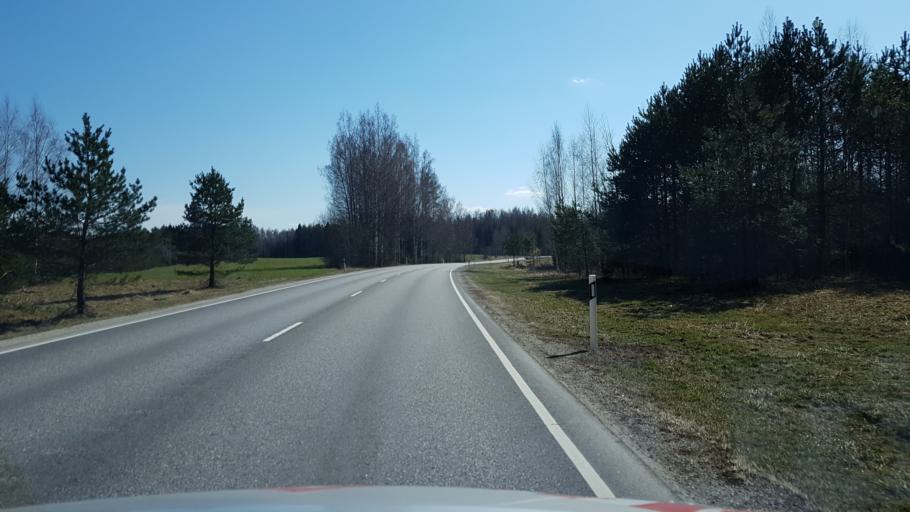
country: EE
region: Jogevamaa
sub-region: Mustvee linn
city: Mustvee
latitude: 58.6998
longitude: 26.8174
